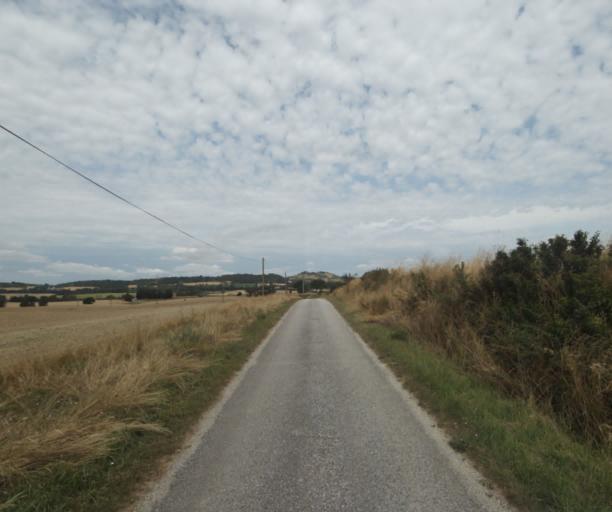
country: FR
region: Midi-Pyrenees
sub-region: Departement de la Haute-Garonne
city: Saint-Felix-Lauragais
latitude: 43.4178
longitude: 1.9061
